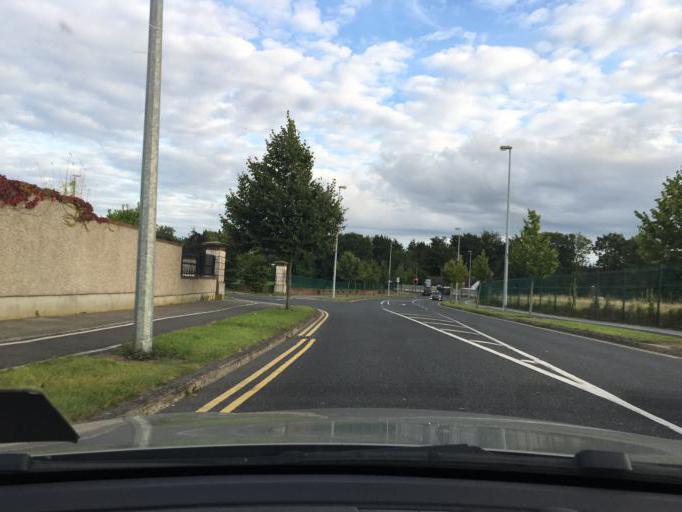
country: IE
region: Leinster
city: Hartstown
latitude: 53.3849
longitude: -6.4194
